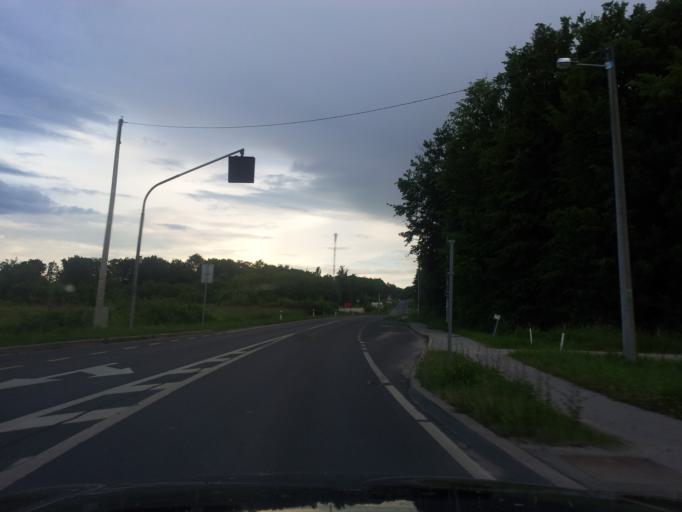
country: HR
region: Zagrebacka
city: Kerestinec
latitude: 45.7334
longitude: 15.7889
